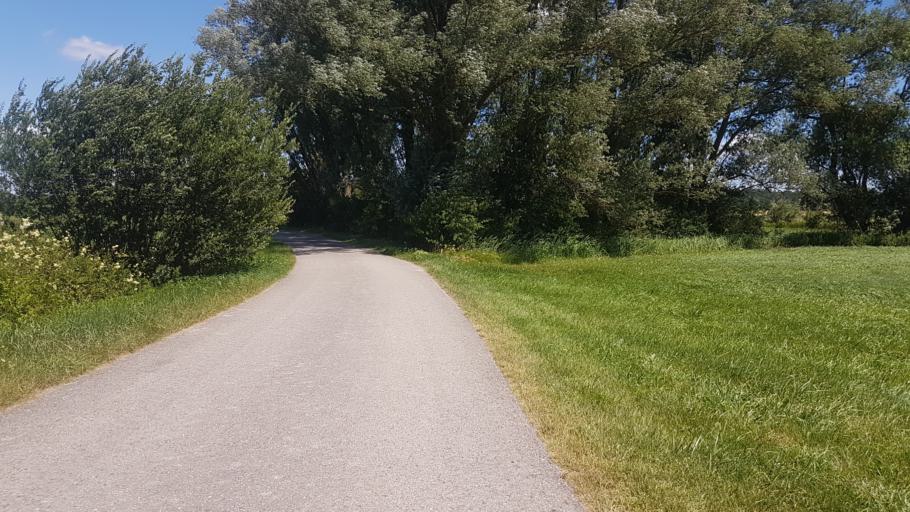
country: DE
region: Bavaria
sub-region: Regierungsbezirk Mittelfranken
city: Aurach
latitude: 49.2756
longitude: 10.4289
